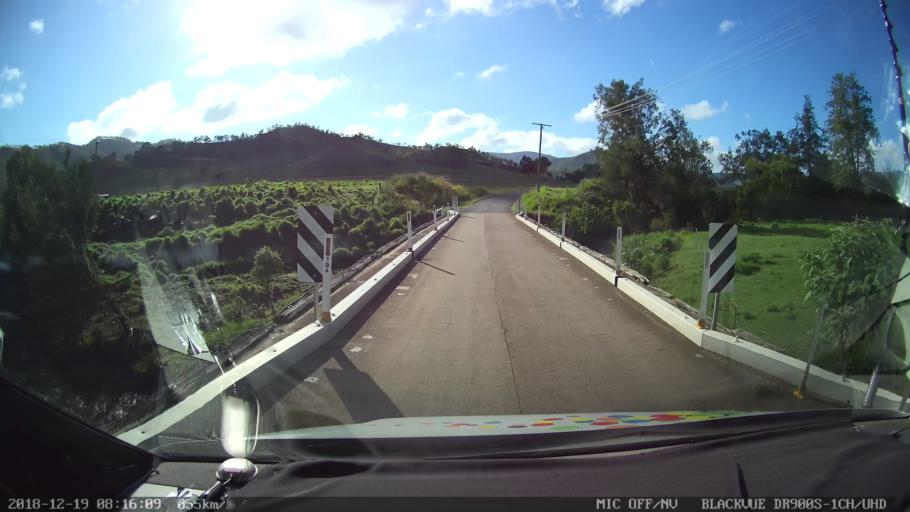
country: AU
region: New South Wales
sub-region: Kyogle
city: Kyogle
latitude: -28.2556
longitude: 152.9052
